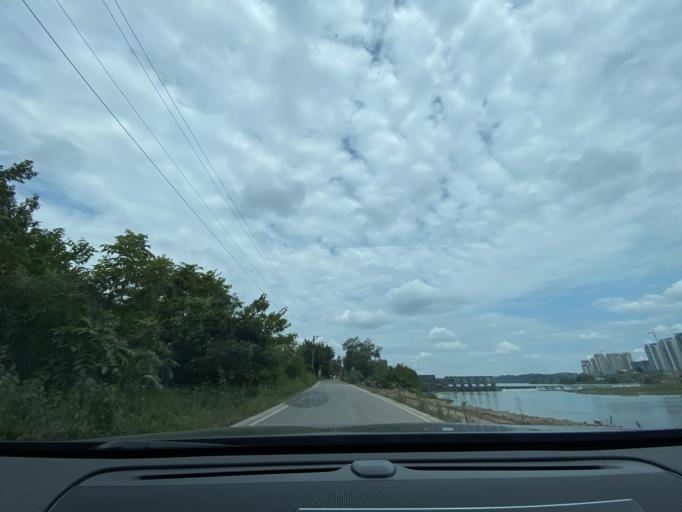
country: CN
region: Sichuan
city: Jiancheng
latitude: 30.4371
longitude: 104.5304
